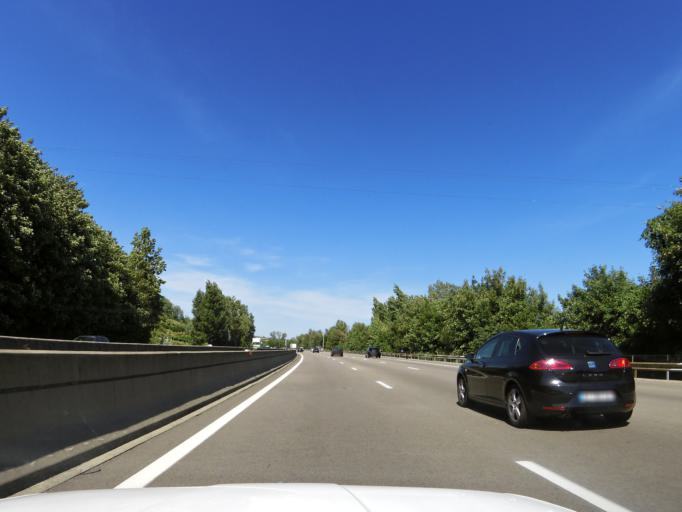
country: FR
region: Rhone-Alpes
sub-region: Departement de la Drome
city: Mercurol
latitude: 45.0870
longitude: 4.8786
